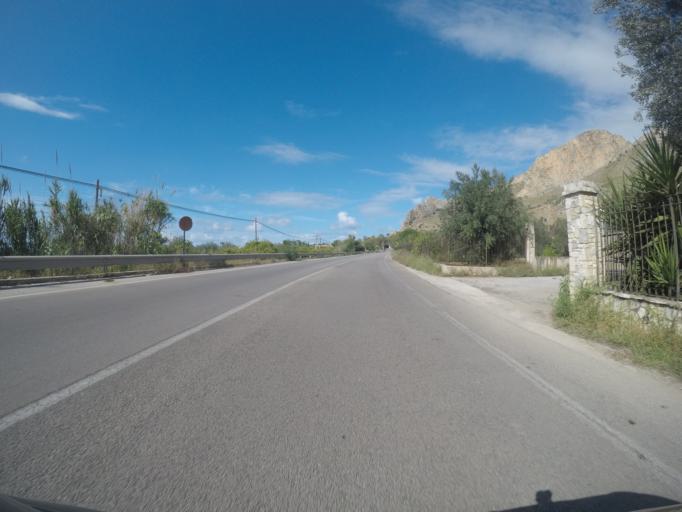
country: IT
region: Sicily
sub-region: Palermo
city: Agliandroni-Paternella
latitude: 38.1188
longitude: 13.0759
